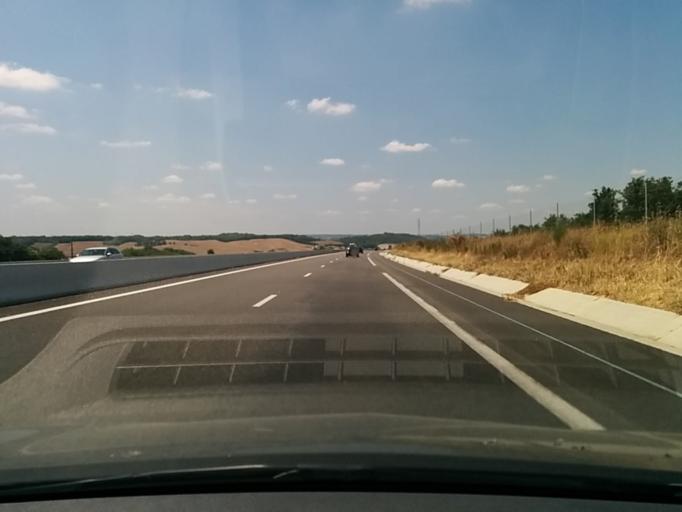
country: FR
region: Midi-Pyrenees
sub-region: Departement du Gers
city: Aubiet
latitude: 43.6480
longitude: 0.6941
